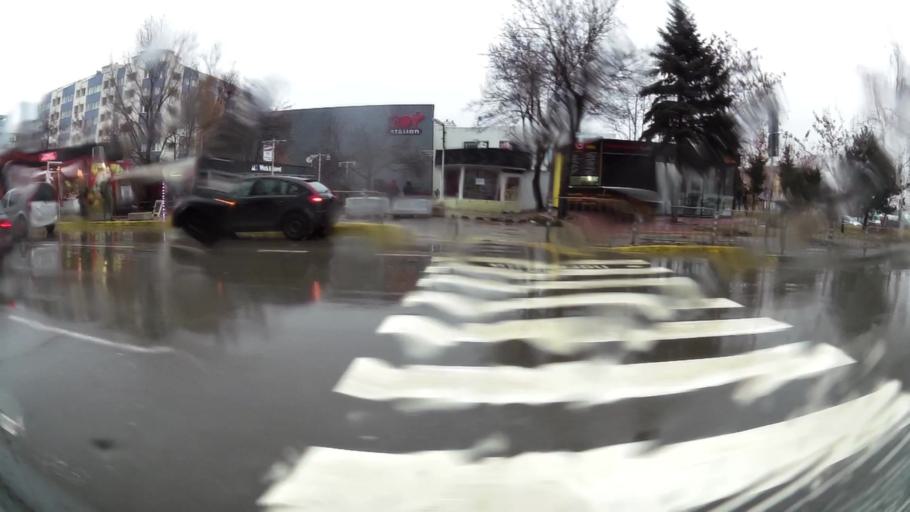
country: BG
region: Sofia-Capital
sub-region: Stolichna Obshtina
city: Sofia
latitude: 42.6536
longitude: 23.3470
